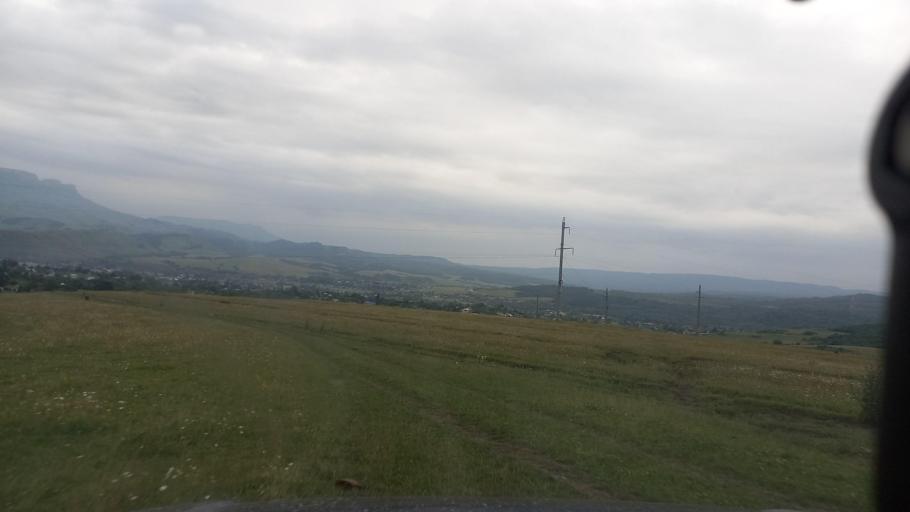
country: RU
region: Karachayevo-Cherkesiya
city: Pregradnaya
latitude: 43.9488
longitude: 41.1637
